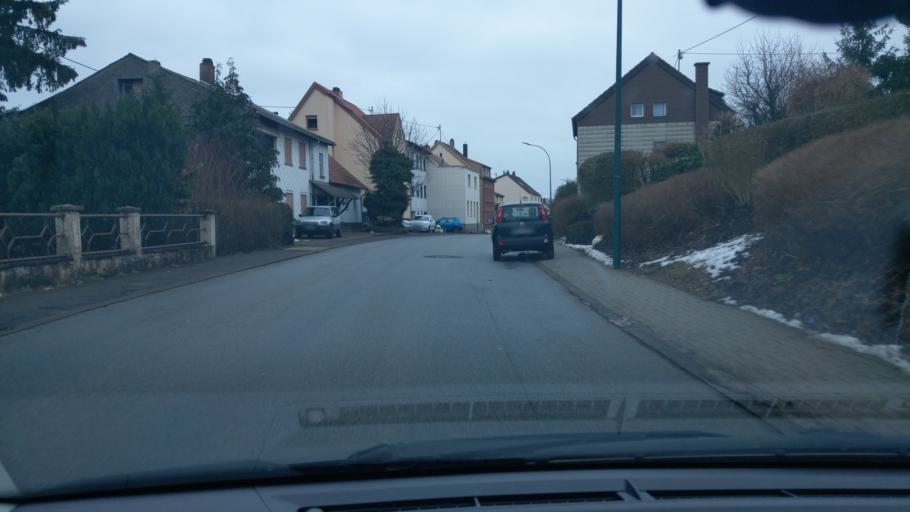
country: DE
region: Saarland
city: Ottweiler
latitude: 49.3749
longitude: 7.1751
